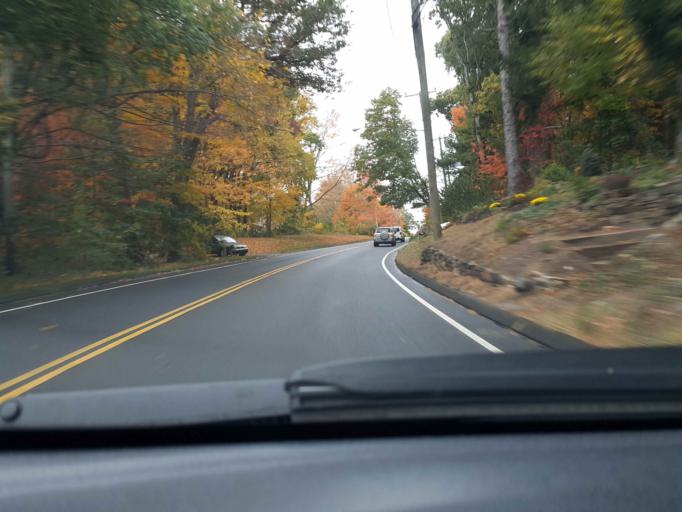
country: US
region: Connecticut
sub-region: New Haven County
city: Guilford Center
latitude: 41.2859
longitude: -72.6506
